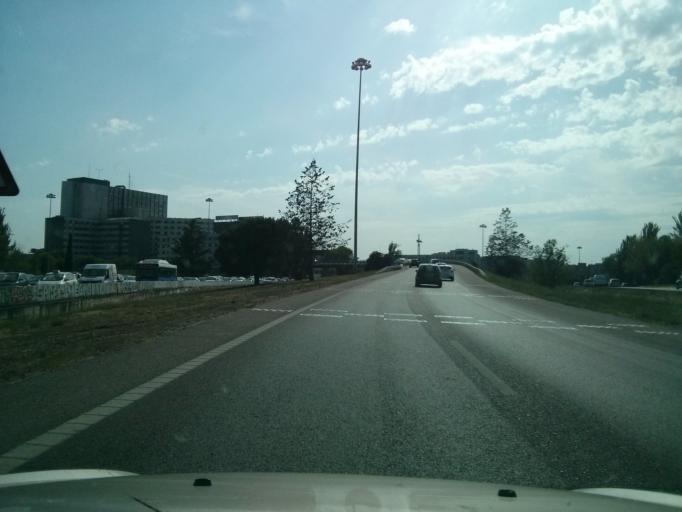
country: ES
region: Madrid
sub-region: Provincia de Madrid
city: Pinar de Chamartin
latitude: 40.4829
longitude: -3.6830
